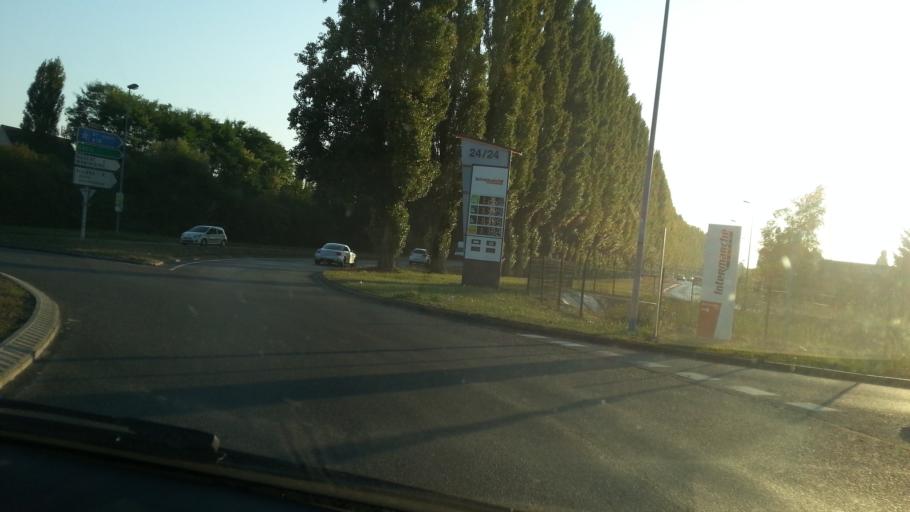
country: FR
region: Picardie
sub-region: Departement de l'Oise
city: Villers-Saint-Paul
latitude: 49.2882
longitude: 2.4990
